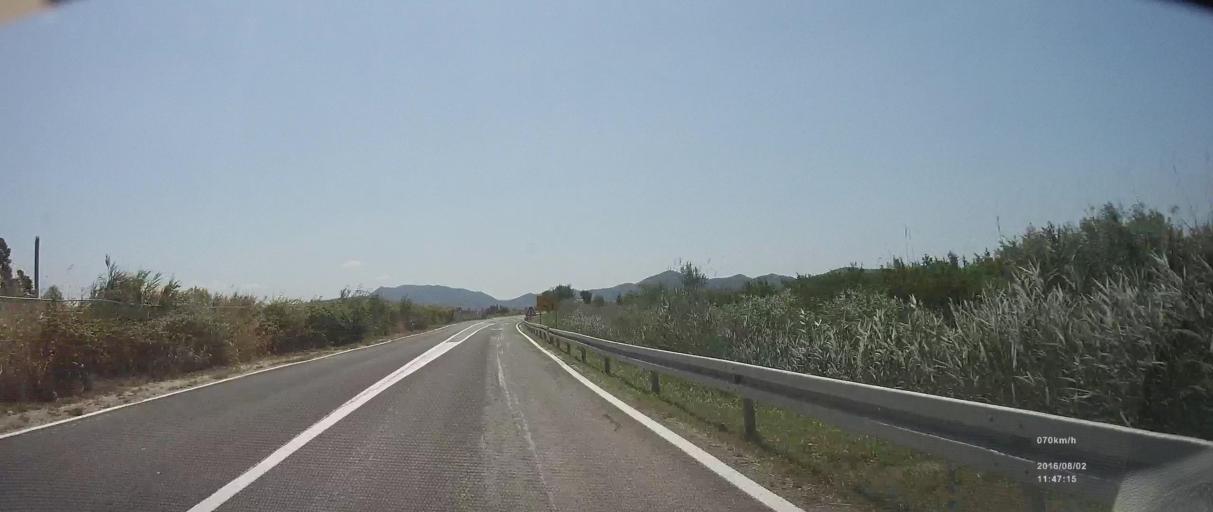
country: HR
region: Dubrovacko-Neretvanska
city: Komin
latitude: 43.0459
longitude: 17.4808
